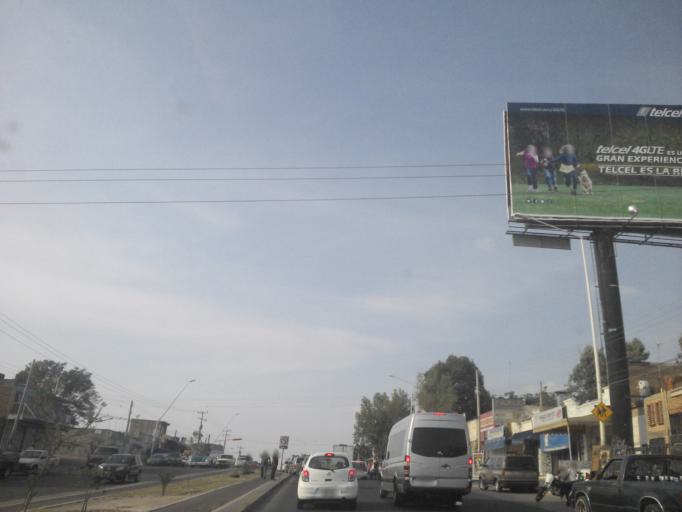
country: MX
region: Jalisco
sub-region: Tlajomulco de Zuniga
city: Altus Bosques
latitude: 20.6054
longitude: -103.3773
